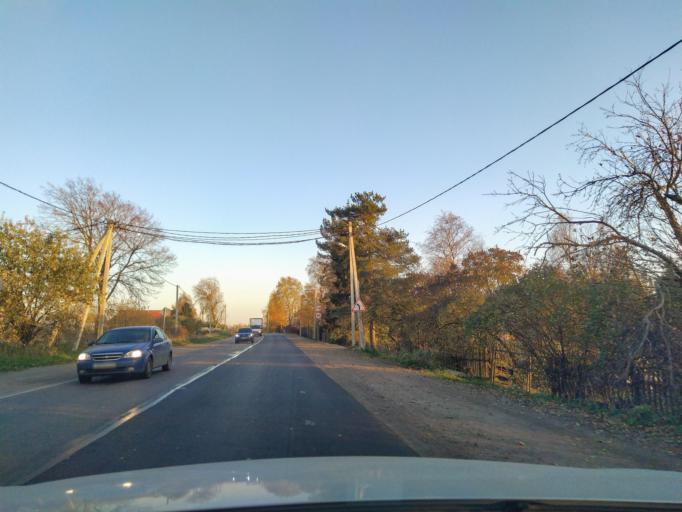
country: RU
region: Leningrad
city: Maloye Verevo
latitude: 59.6136
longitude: 30.2205
